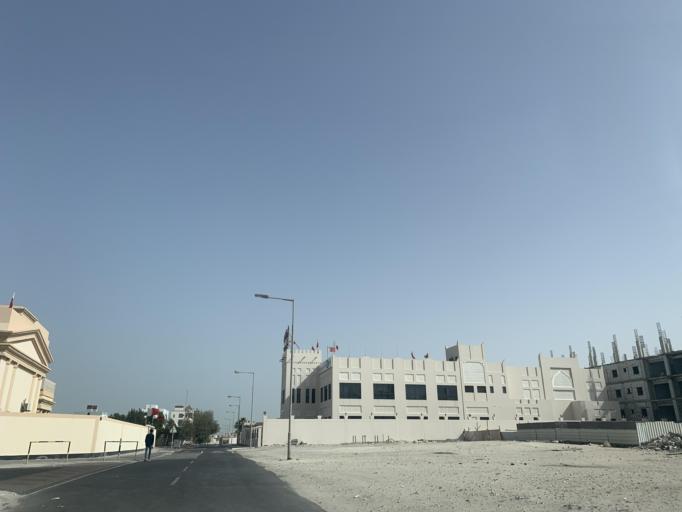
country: BH
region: Northern
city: Ar Rifa'
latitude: 26.1530
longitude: 50.5676
